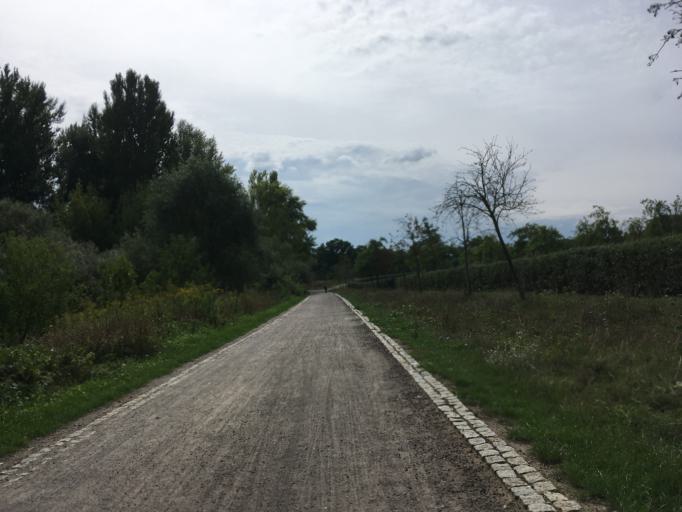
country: DE
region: Berlin
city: Kaulsdorf
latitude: 52.5158
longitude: 13.5732
